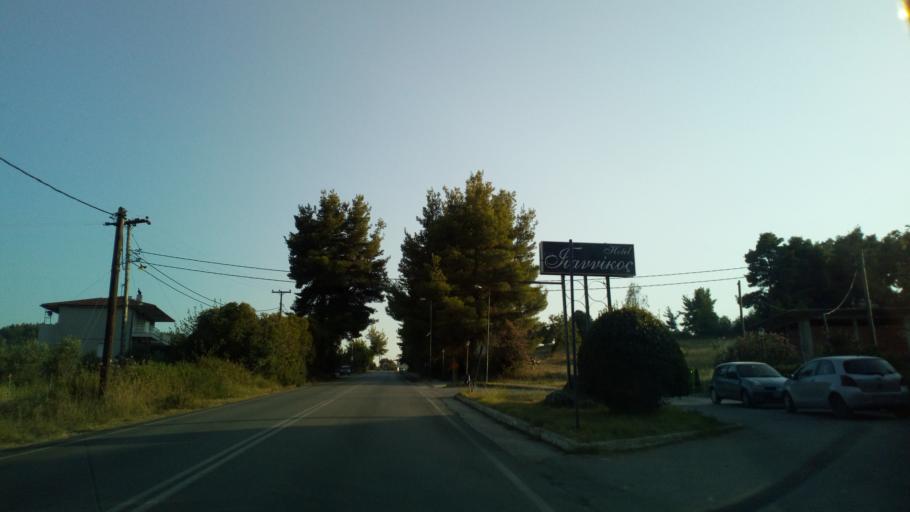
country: GR
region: Central Macedonia
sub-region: Nomos Chalkidikis
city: Pefkochori
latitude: 39.9463
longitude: 23.6740
